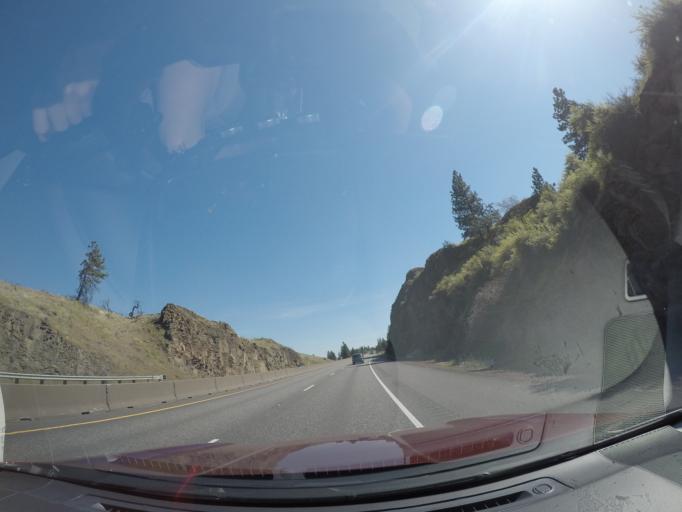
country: US
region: Oregon
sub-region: Wasco County
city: Chenoweth
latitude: 45.6638
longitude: -121.2205
